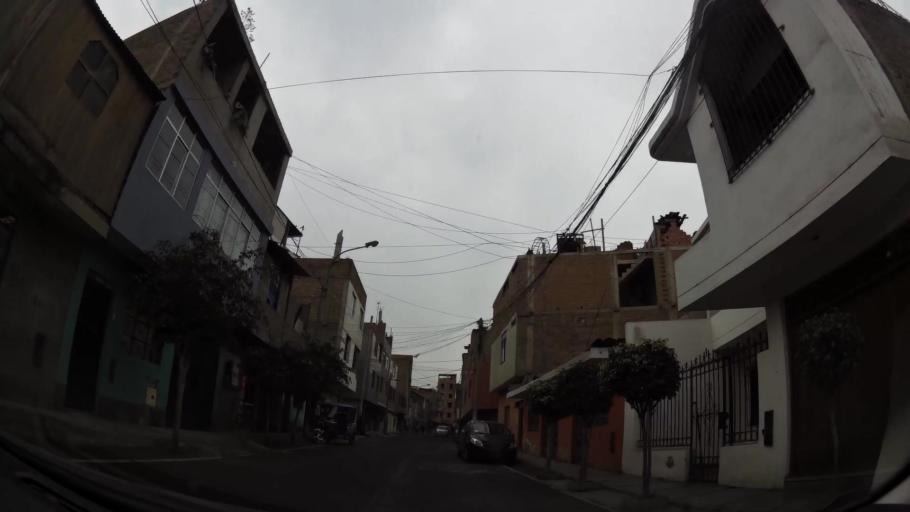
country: PE
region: Lima
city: Lima
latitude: -12.0496
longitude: -77.0028
